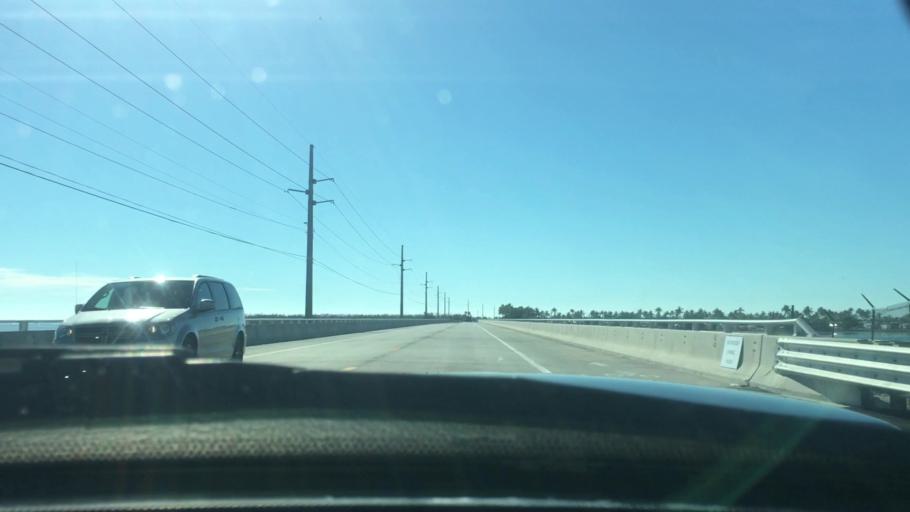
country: US
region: Florida
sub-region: Monroe County
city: Big Pine Key
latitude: 24.6760
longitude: -81.2399
